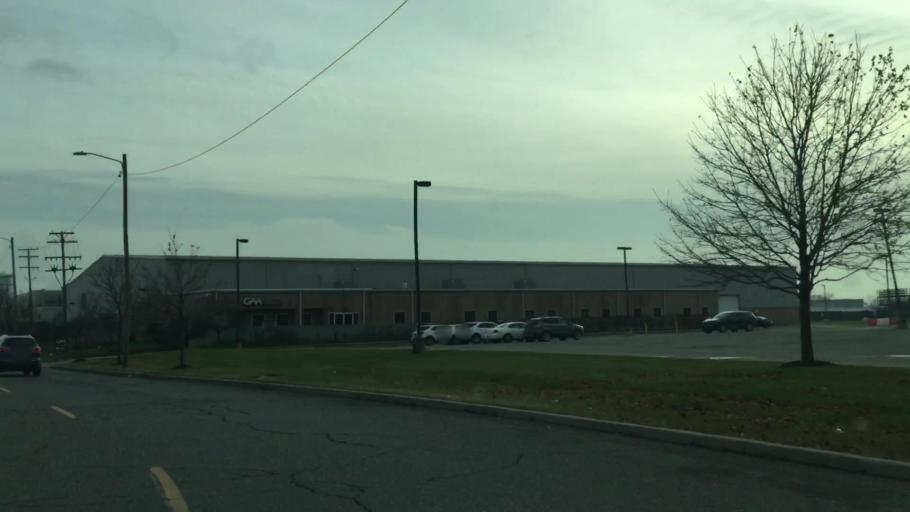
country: US
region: Michigan
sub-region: Wayne County
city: Detroit
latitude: 42.3302
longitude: -83.1029
